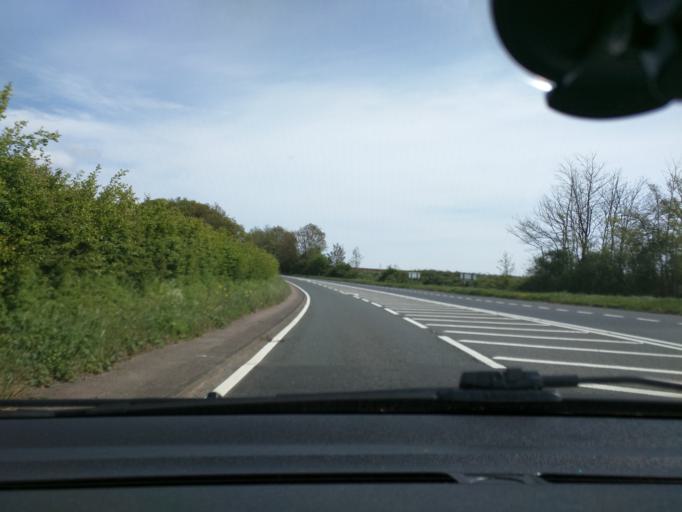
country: GB
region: England
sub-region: Suffolk
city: Saxmundham
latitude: 52.2684
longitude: 1.5177
